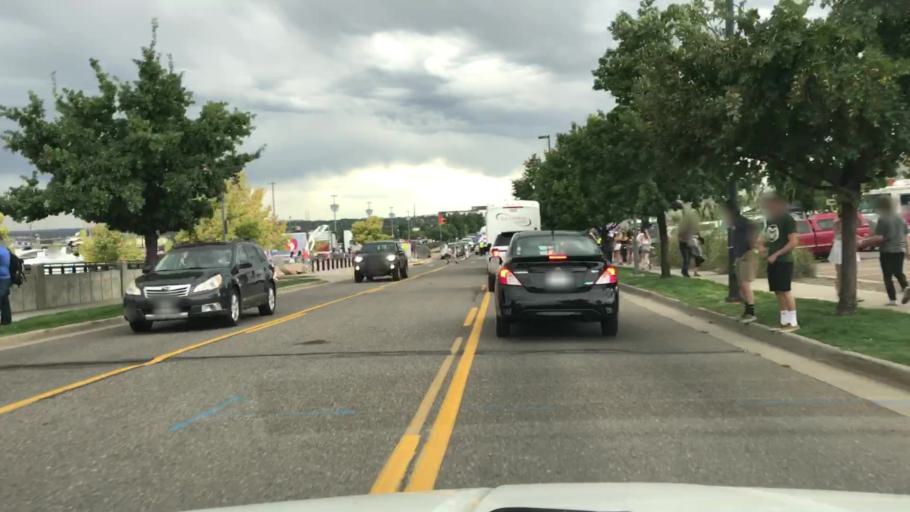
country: US
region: Colorado
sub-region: Denver County
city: Denver
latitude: 39.7447
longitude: -105.0237
